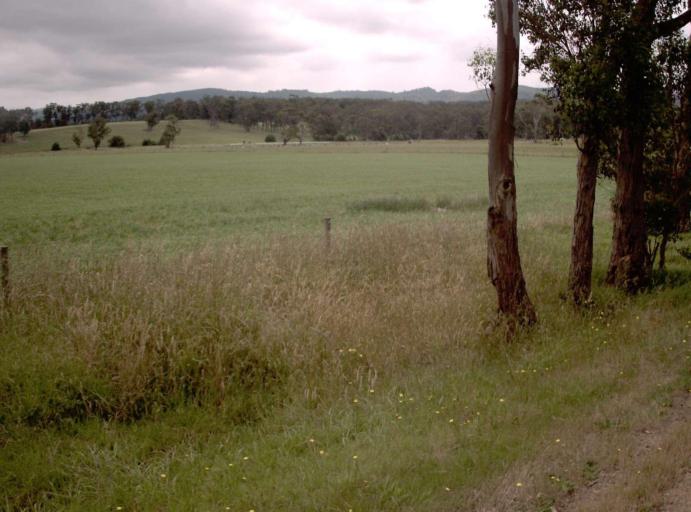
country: AU
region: Victoria
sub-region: Latrobe
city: Traralgon
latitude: -38.4923
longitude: 146.6795
